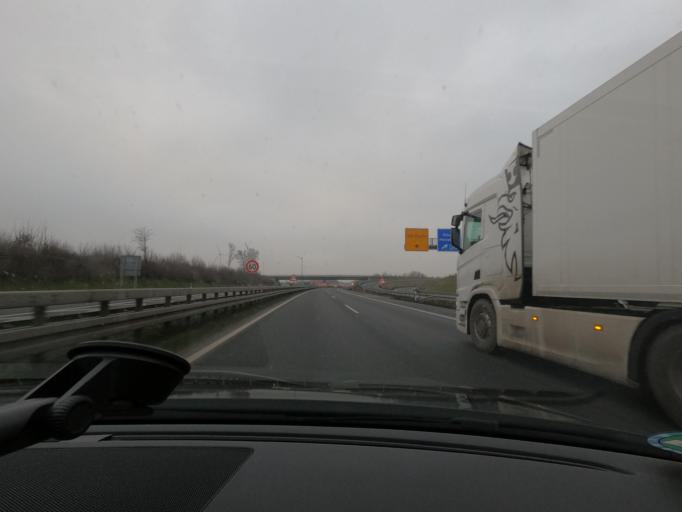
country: DE
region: North Rhine-Westphalia
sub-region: Regierungsbezirk Dusseldorf
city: Juchen
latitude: 51.1066
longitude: 6.4281
